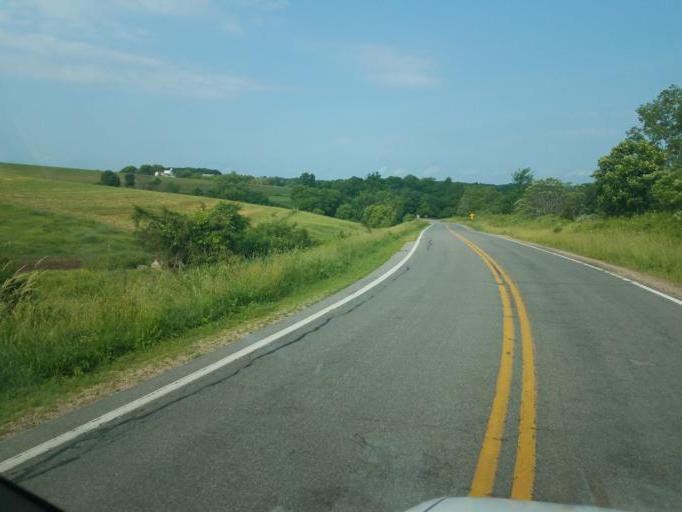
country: US
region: Wisconsin
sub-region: Vernon County
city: Hillsboro
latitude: 43.6750
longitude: -90.4717
